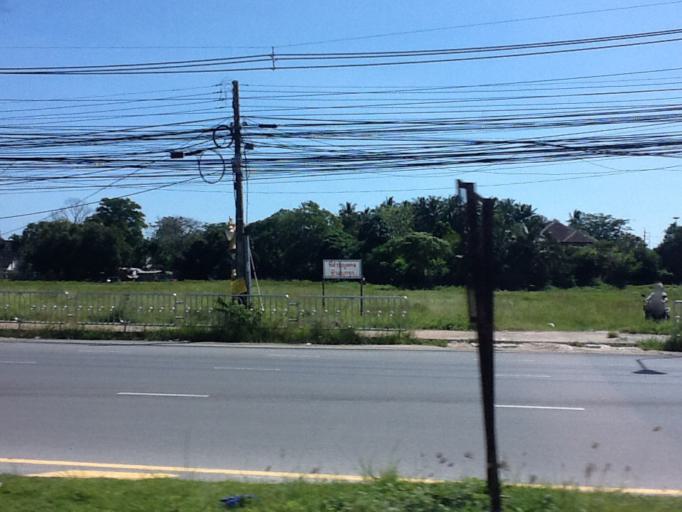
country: TH
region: Phuket
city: Ban Ko Kaeo
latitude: 7.9814
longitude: 98.3645
